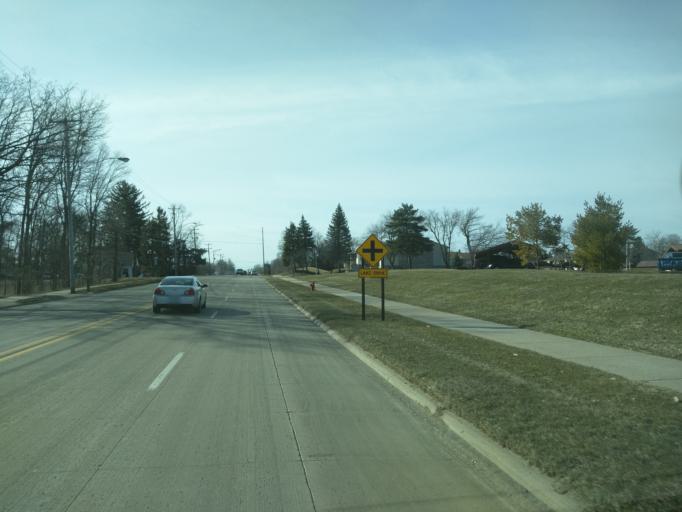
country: US
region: Michigan
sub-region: Ingham County
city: Haslett
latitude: 42.7505
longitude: -84.4085
